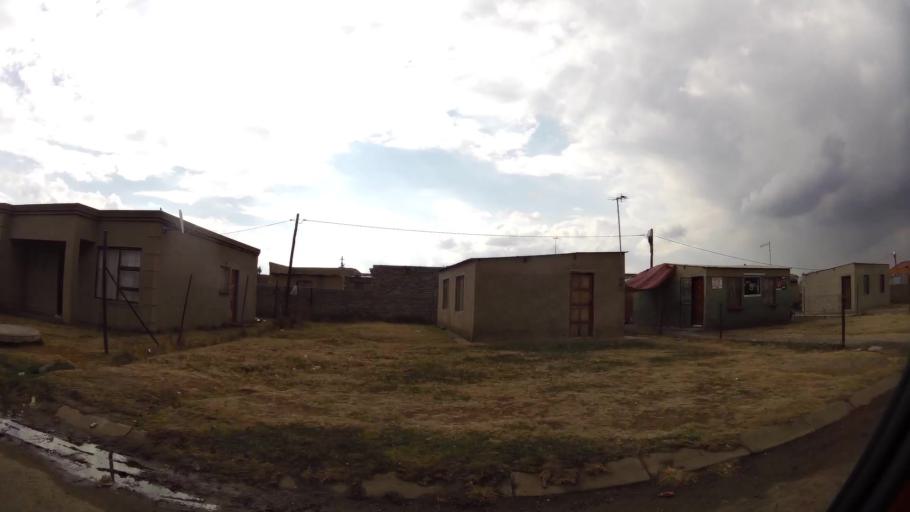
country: ZA
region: Gauteng
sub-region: Sedibeng District Municipality
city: Vanderbijlpark
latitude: -26.6887
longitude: 27.7809
